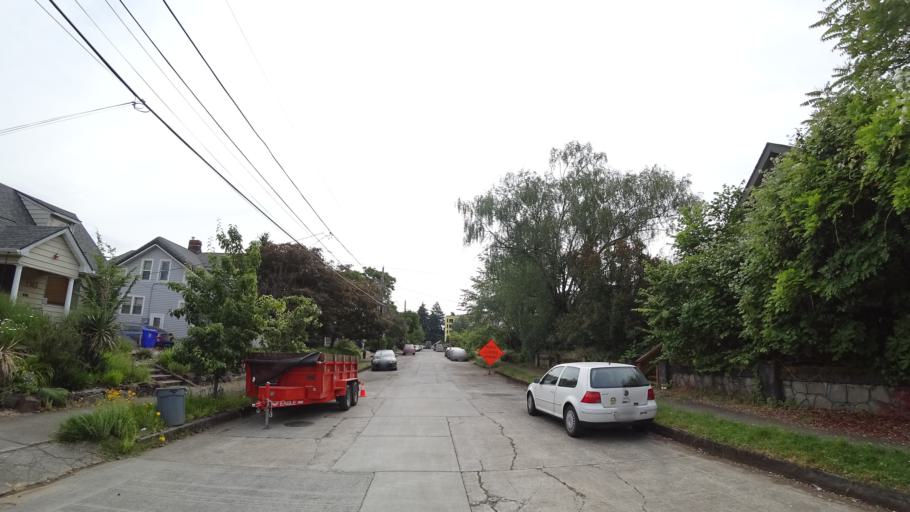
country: US
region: Oregon
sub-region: Multnomah County
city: Portland
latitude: 45.5677
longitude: -122.6851
